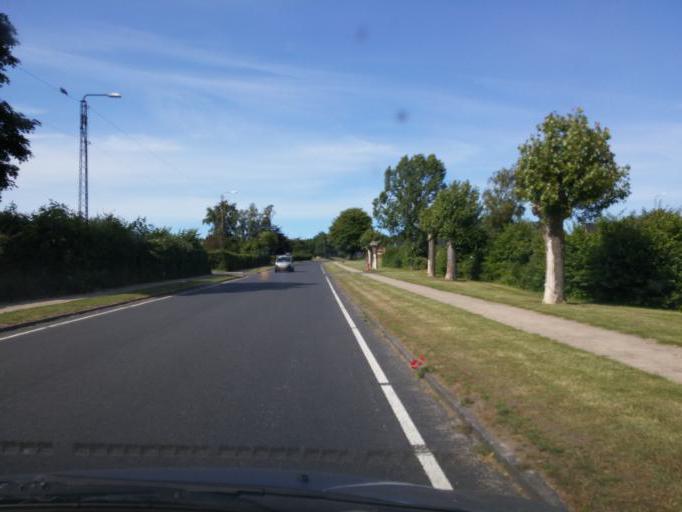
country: DK
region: South Denmark
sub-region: Kerteminde Kommune
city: Munkebo
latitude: 55.4632
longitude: 10.5627
